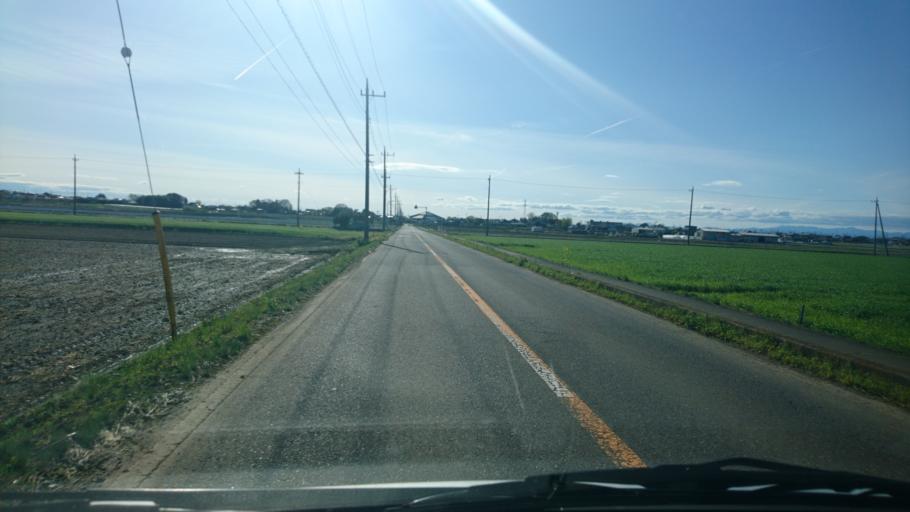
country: JP
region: Ibaraki
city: Yuki
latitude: 36.2816
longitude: 139.8908
